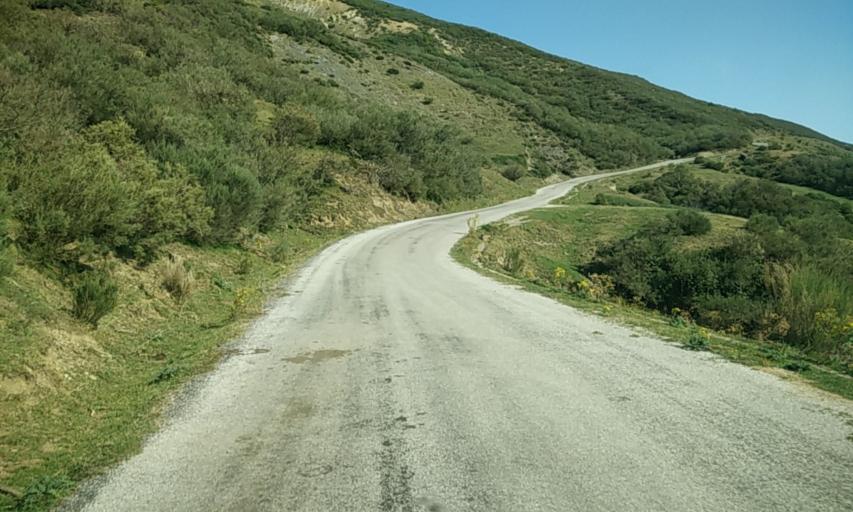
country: ES
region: Cantabria
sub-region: Provincia de Cantabria
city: Camaleno
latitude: 43.0692
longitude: -4.7628
